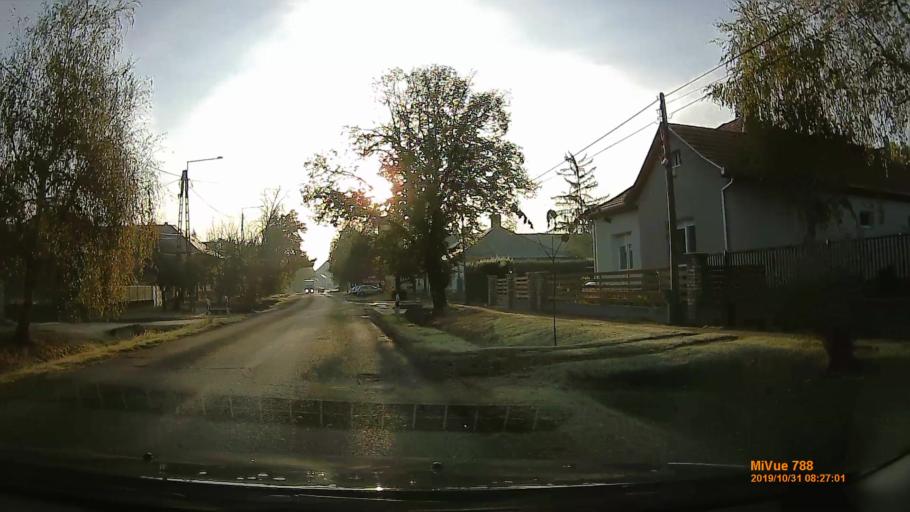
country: HU
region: Pest
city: Tapiobicske
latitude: 47.3639
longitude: 19.6834
